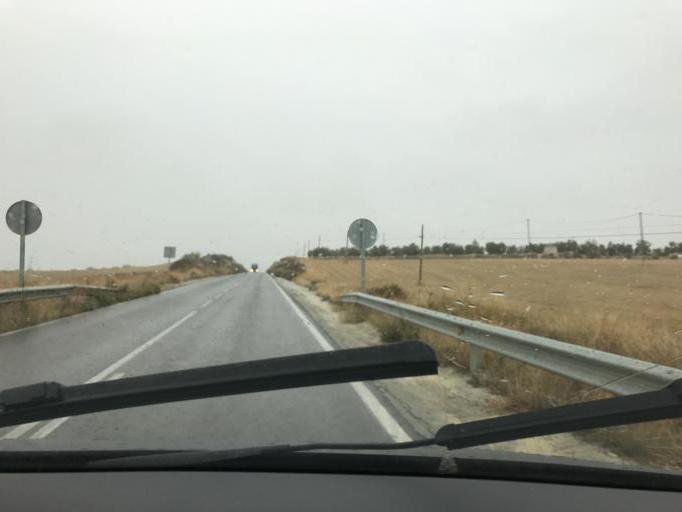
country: ES
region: Andalusia
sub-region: Provincia de Granada
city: Escuzar
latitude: 37.0906
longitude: -3.7389
